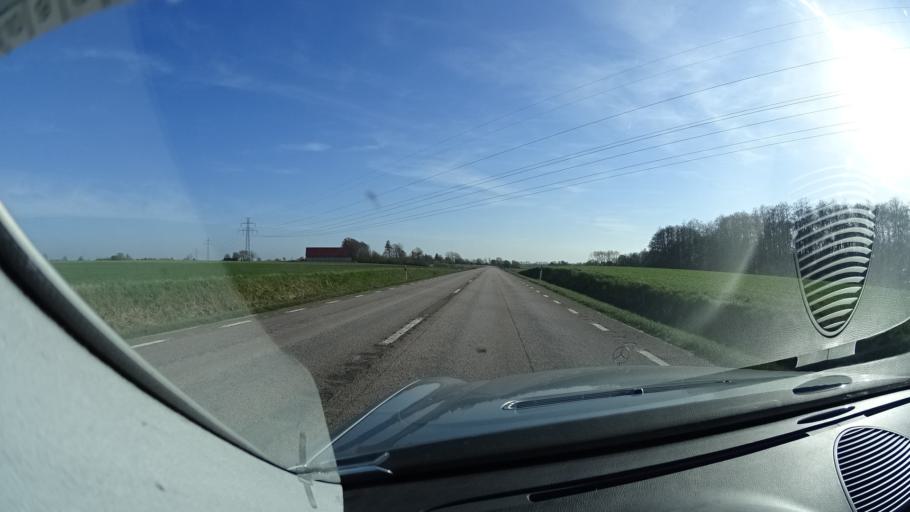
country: SE
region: Skane
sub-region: Bjuvs Kommun
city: Billesholm
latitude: 55.9873
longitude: 12.9394
